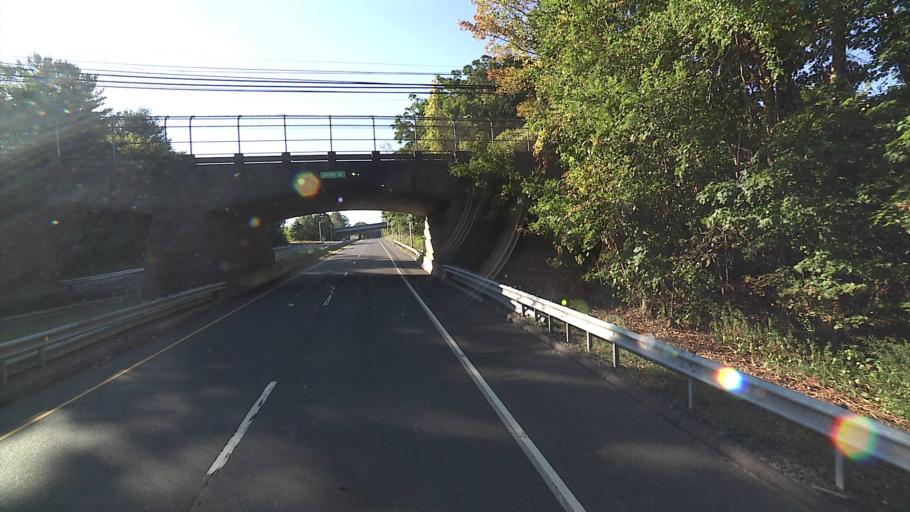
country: US
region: Connecticut
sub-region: New Haven County
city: Meriden
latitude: 41.5424
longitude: -72.7714
